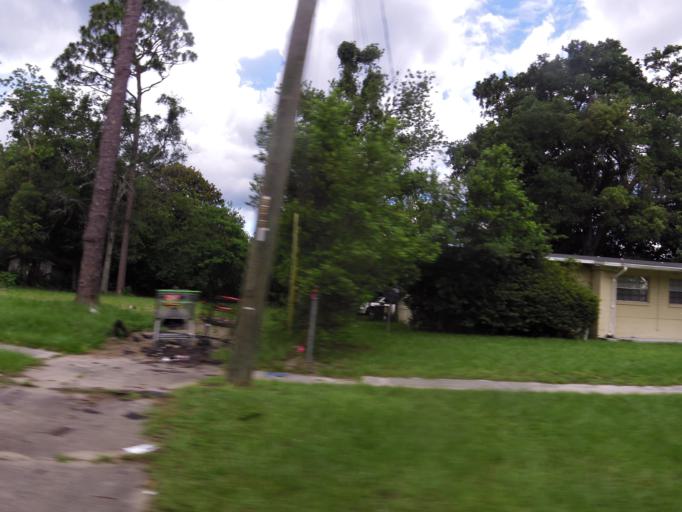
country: US
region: Florida
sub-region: Duval County
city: Jacksonville
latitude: 30.4240
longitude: -81.6643
